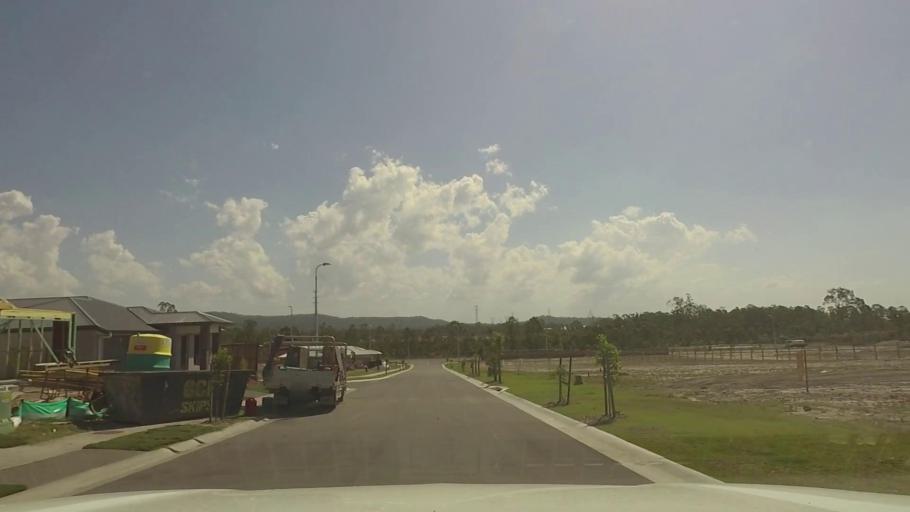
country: AU
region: Queensland
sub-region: Logan
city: Chambers Flat
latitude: -27.8150
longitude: 153.1293
